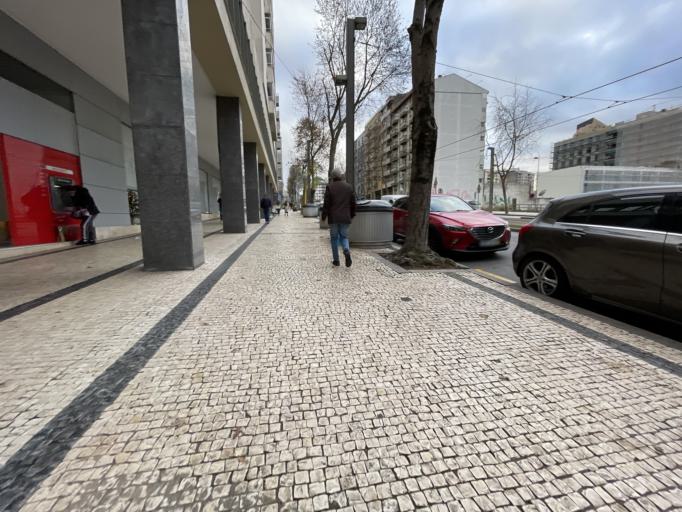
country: PT
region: Porto
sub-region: Vila Nova de Gaia
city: Vila Nova de Gaia
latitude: 41.1317
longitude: -8.6070
